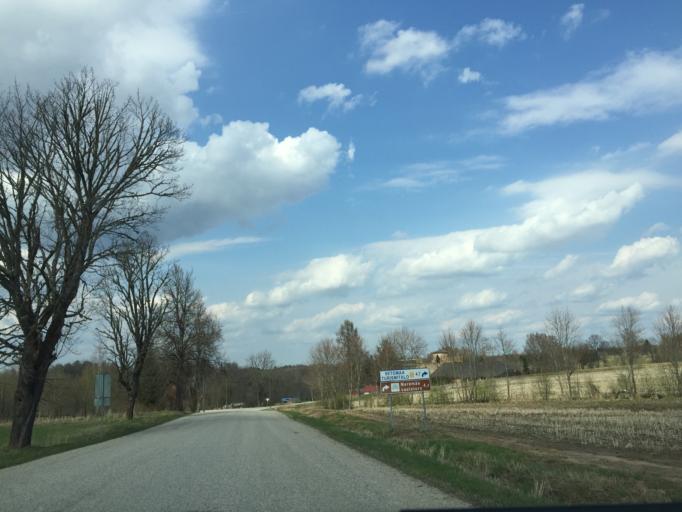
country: RU
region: Pskov
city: Pechory
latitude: 57.7263
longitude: 27.3587
